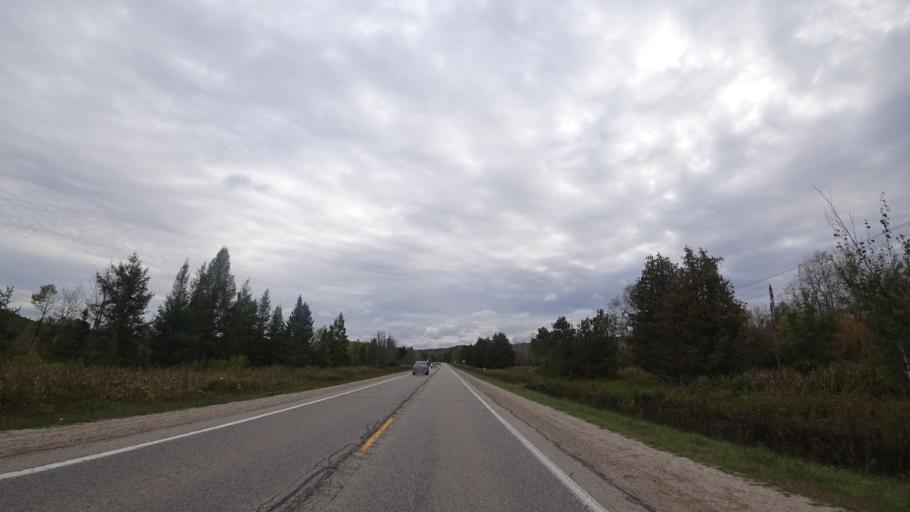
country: US
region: Michigan
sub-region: Charlevoix County
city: Boyne City
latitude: 45.2217
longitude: -84.9220
